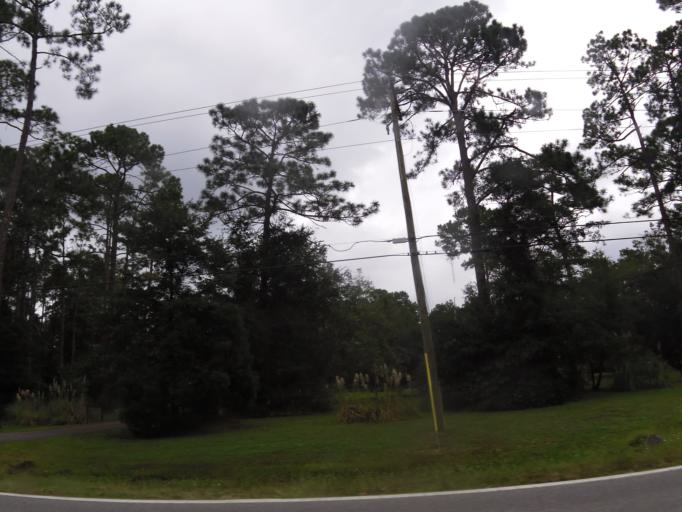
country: US
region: Florida
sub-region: Clay County
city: Middleburg
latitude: 30.1142
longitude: -81.8599
